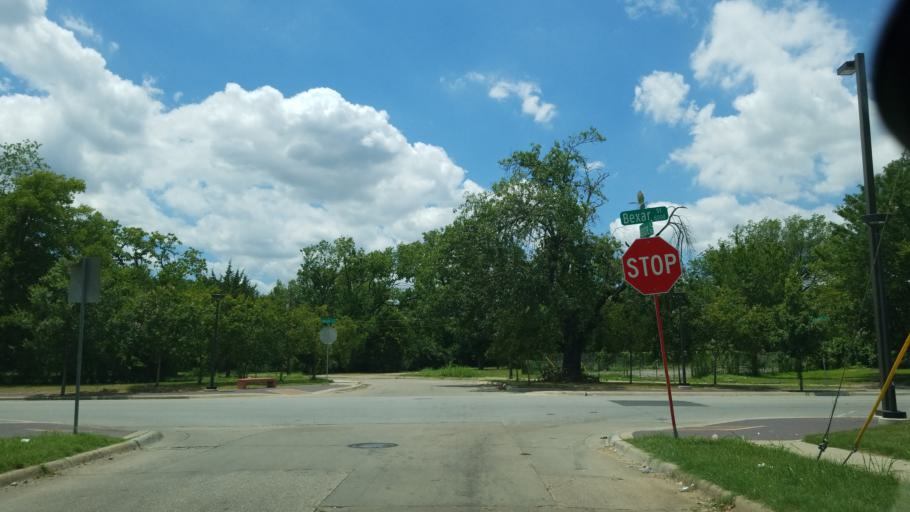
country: US
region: Texas
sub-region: Dallas County
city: Dallas
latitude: 32.7419
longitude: -96.7531
